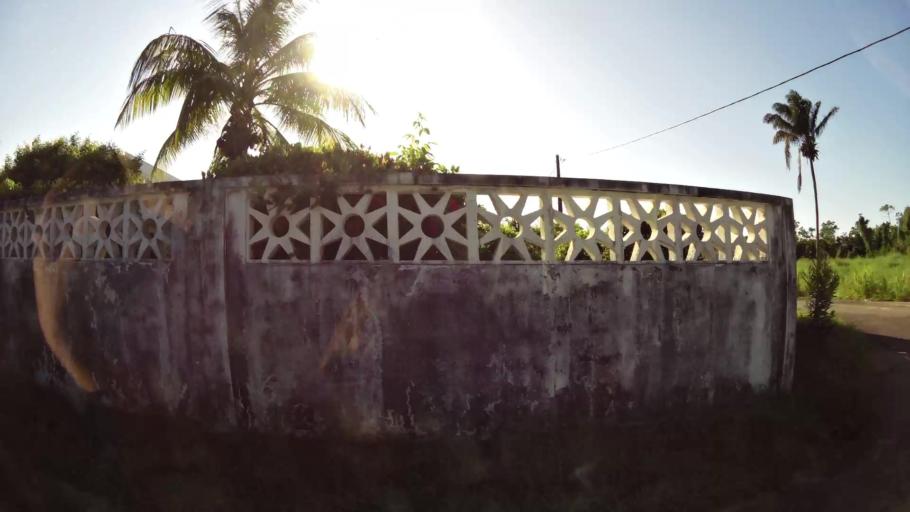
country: GF
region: Guyane
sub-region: Guyane
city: Remire-Montjoly
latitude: 4.8993
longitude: -52.2769
